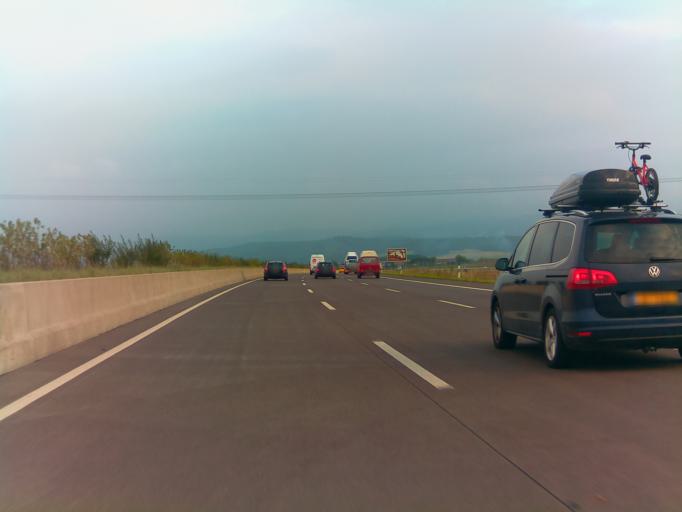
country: DE
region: Thuringia
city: Haina
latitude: 50.9715
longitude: 10.4882
